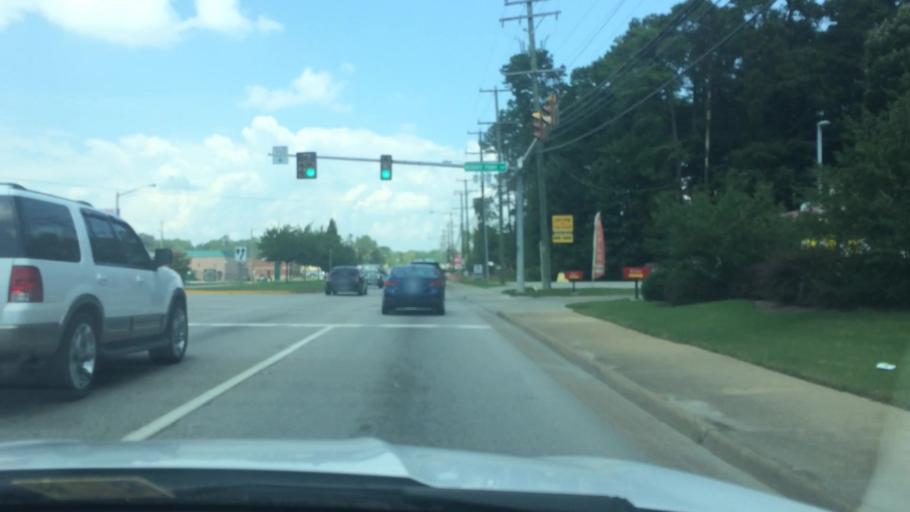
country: US
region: Virginia
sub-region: York County
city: Yorktown
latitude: 37.1561
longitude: -76.5558
